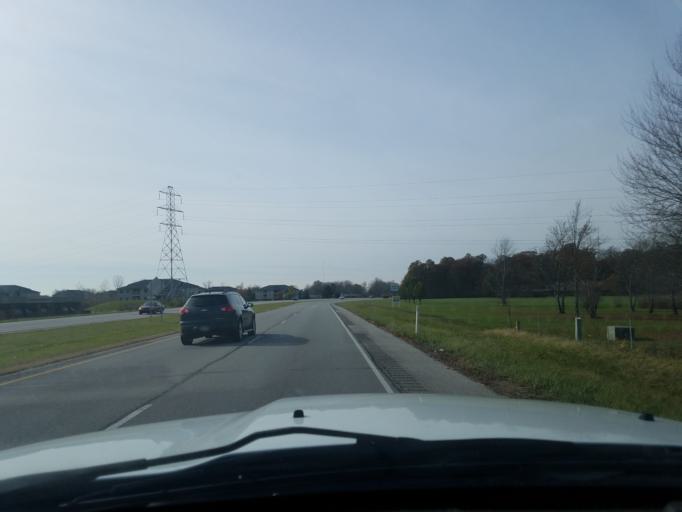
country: US
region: Indiana
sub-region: Delaware County
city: Muncie
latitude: 40.2176
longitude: -85.4458
